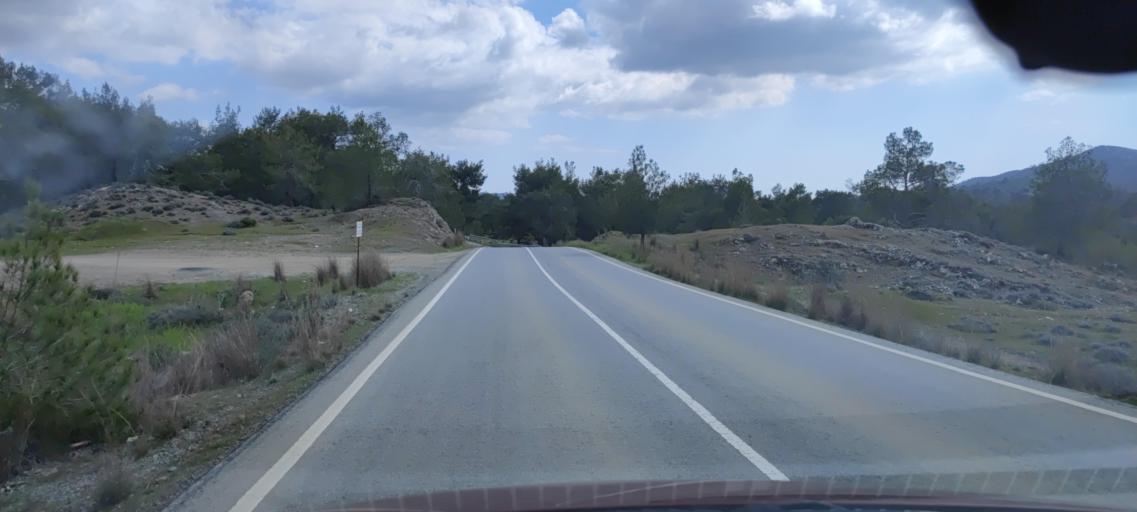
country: CY
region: Larnaka
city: Kornos
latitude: 34.9222
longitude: 33.3491
